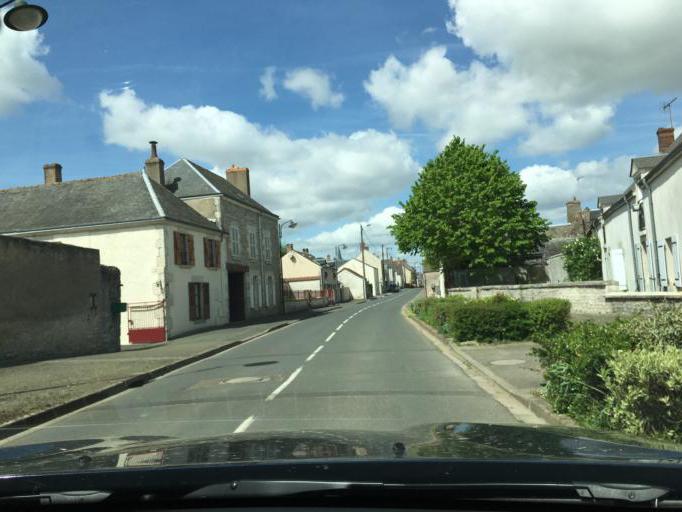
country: FR
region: Centre
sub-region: Departement du Loiret
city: Bricy
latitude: 48.0518
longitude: 1.7937
